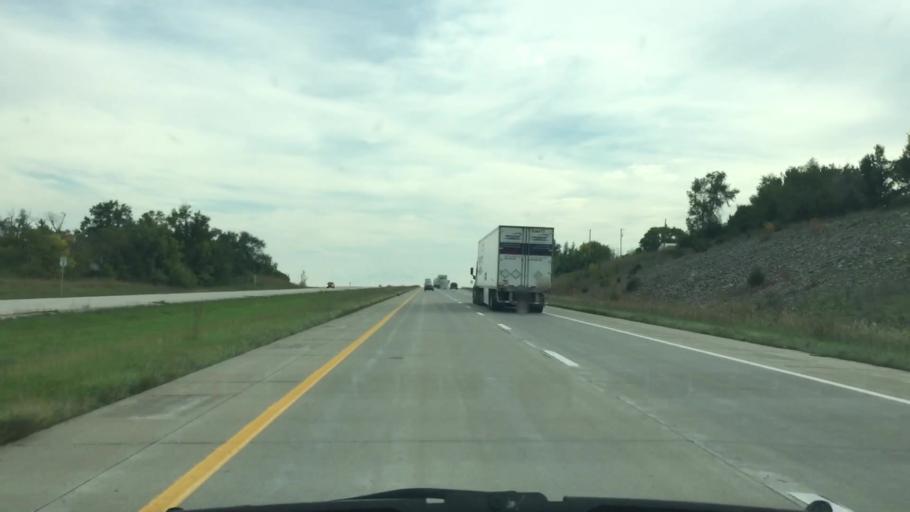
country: US
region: Missouri
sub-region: Harrison County
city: Bethany
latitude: 40.2867
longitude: -94.0125
